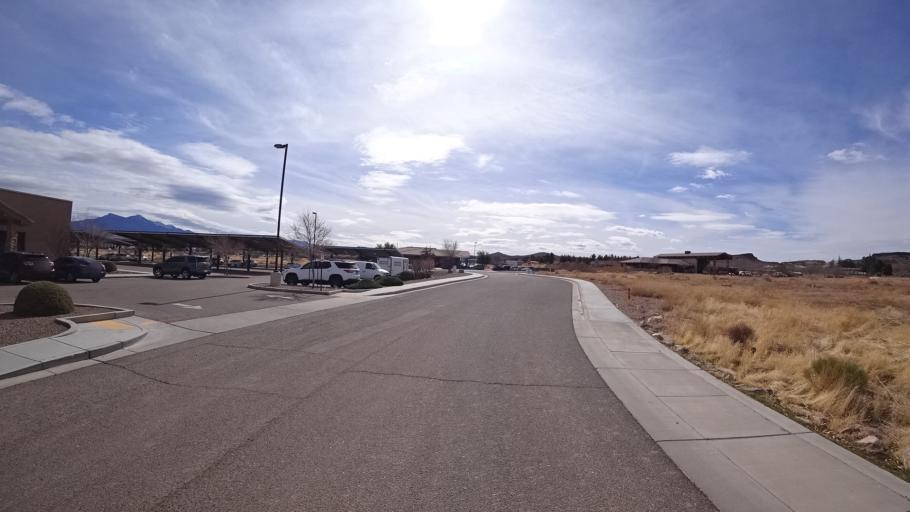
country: US
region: Arizona
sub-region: Mohave County
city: Kingman
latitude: 35.2257
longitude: -114.0426
